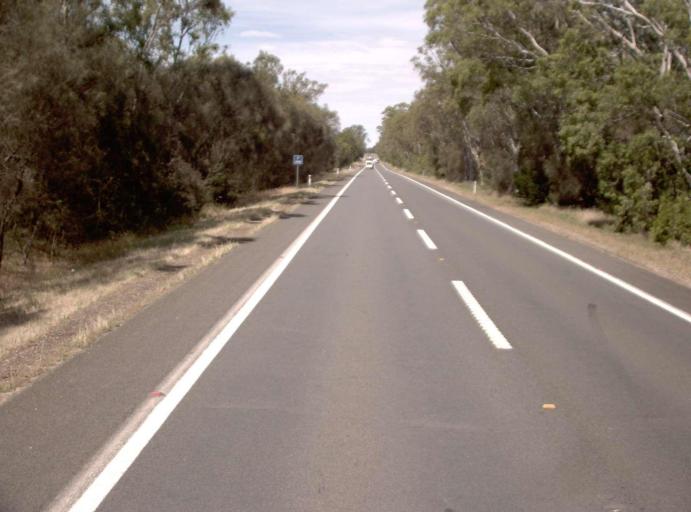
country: AU
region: Victoria
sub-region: Wellington
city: Sale
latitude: -37.9512
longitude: 147.1108
